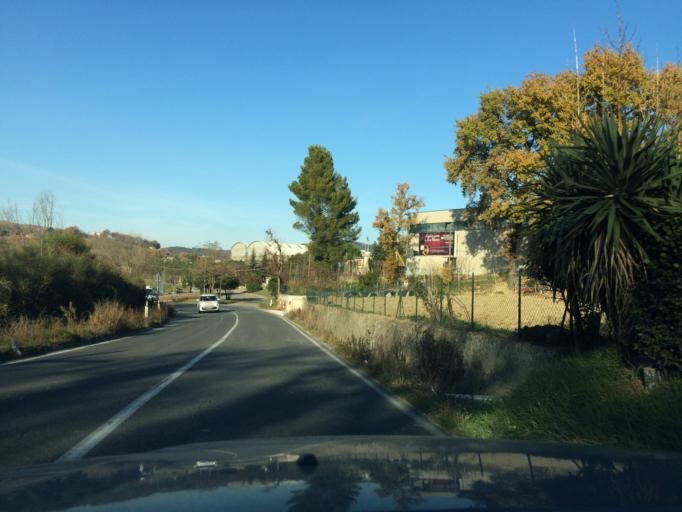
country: IT
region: Umbria
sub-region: Provincia di Terni
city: Fornole
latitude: 42.5470
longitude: 12.4488
